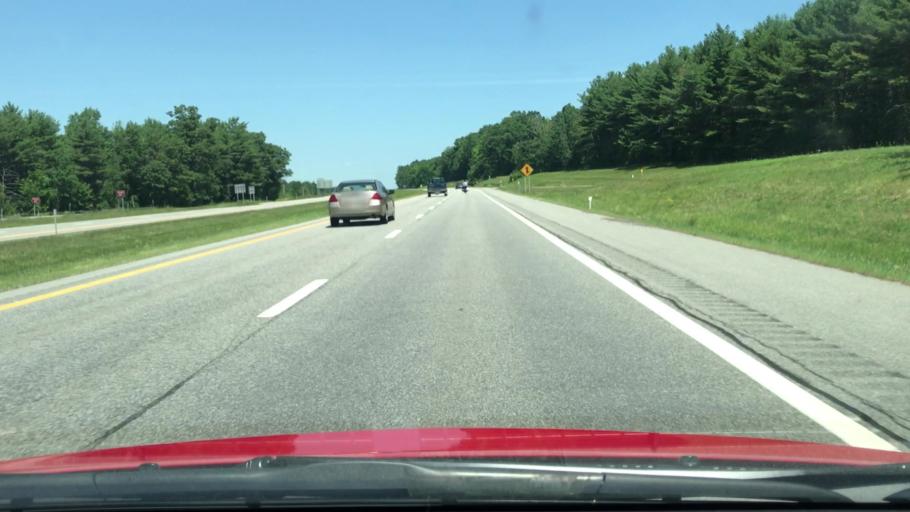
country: US
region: New York
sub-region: Essex County
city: Keeseville
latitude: 44.4455
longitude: -73.4904
